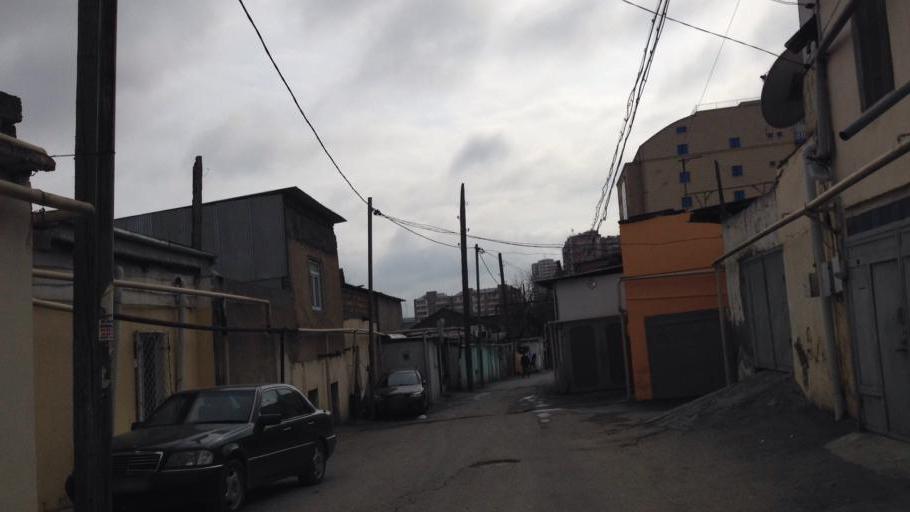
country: AZ
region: Baki
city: Bilajari
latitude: 40.3995
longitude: 49.8282
